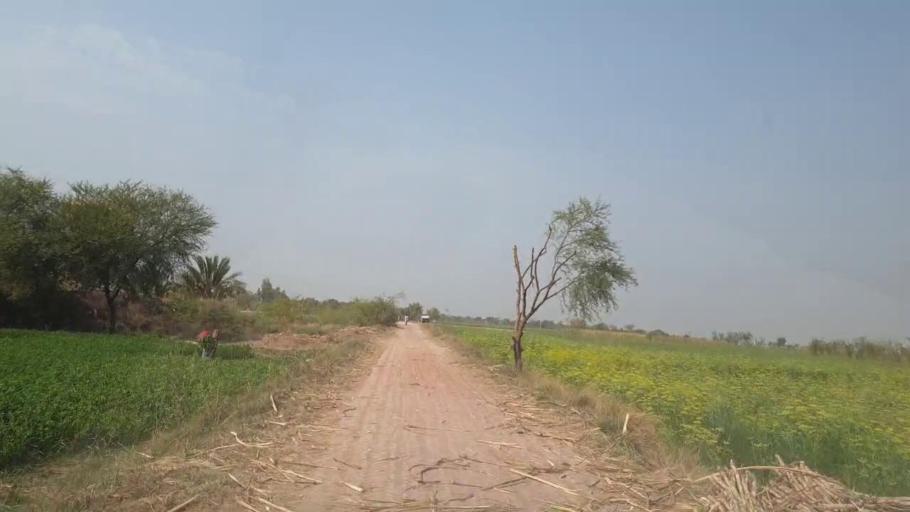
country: PK
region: Sindh
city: Mirpur Khas
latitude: 25.5789
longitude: 69.1356
